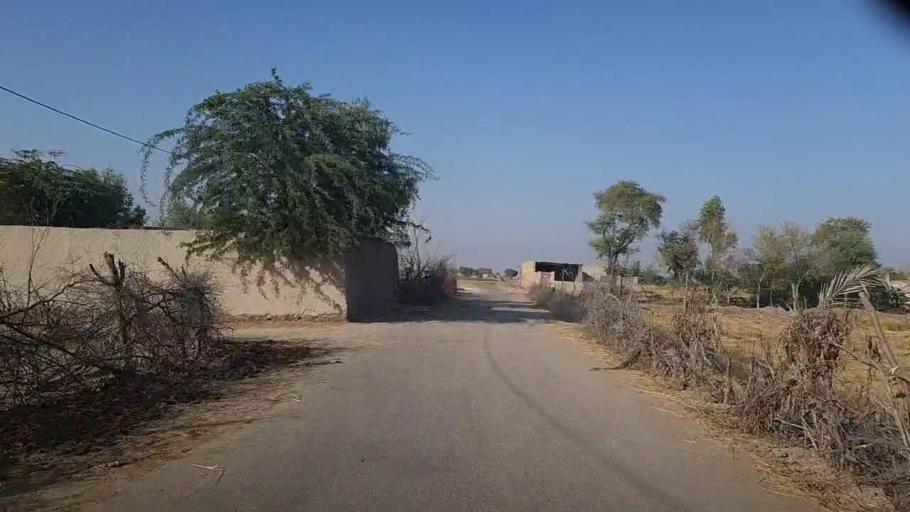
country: PK
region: Sindh
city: Tangwani
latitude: 28.2937
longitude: 68.9505
